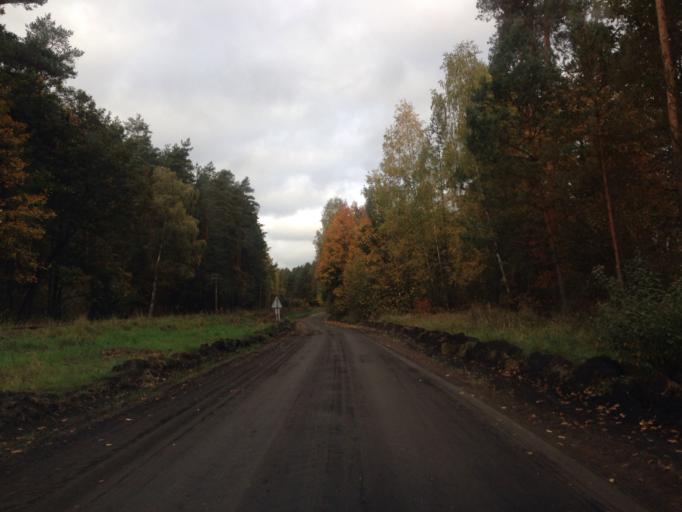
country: PL
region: Kujawsko-Pomorskie
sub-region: Powiat brodnicki
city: Bartniczka
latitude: 53.2665
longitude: 19.5806
